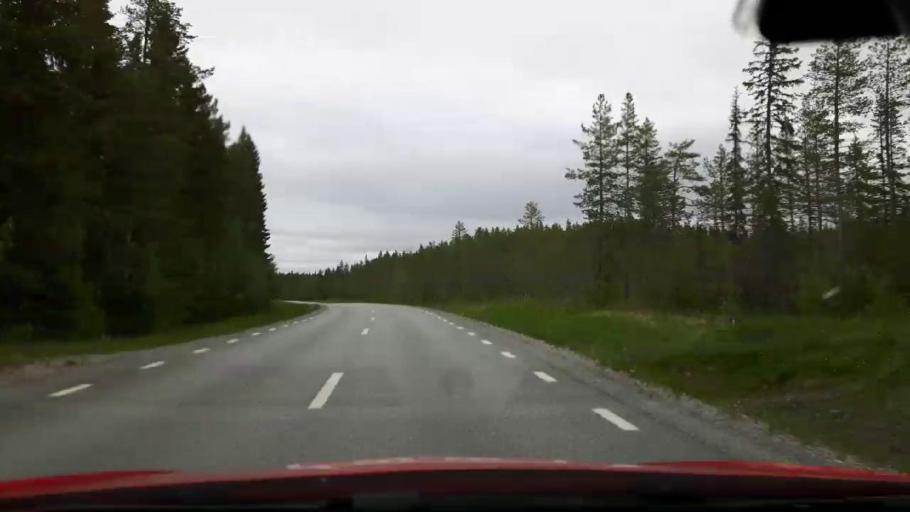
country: SE
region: Jaemtland
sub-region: OEstersunds Kommun
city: Lit
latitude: 63.6939
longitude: 14.6827
